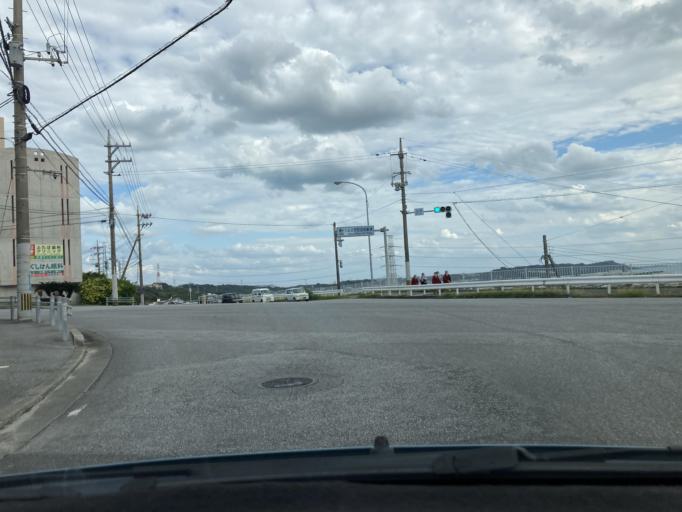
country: JP
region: Okinawa
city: Gushikawa
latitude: 26.3501
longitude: 127.8375
